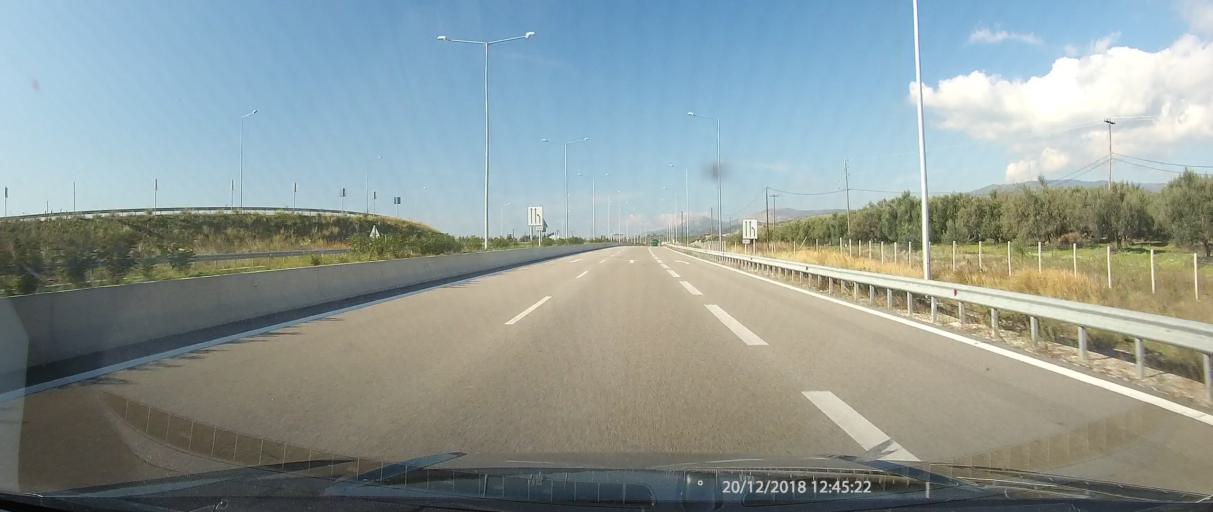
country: GR
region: West Greece
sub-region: Nomos Aitolias kai Akarnanias
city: Mesolongi
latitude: 38.3800
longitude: 21.4980
